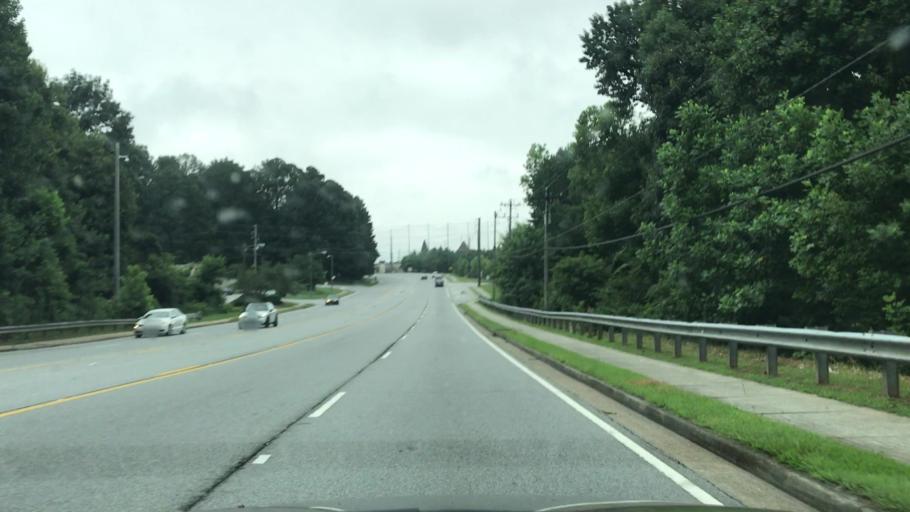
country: US
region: Georgia
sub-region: Gwinnett County
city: Berkeley Lake
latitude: 33.9409
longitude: -84.1653
